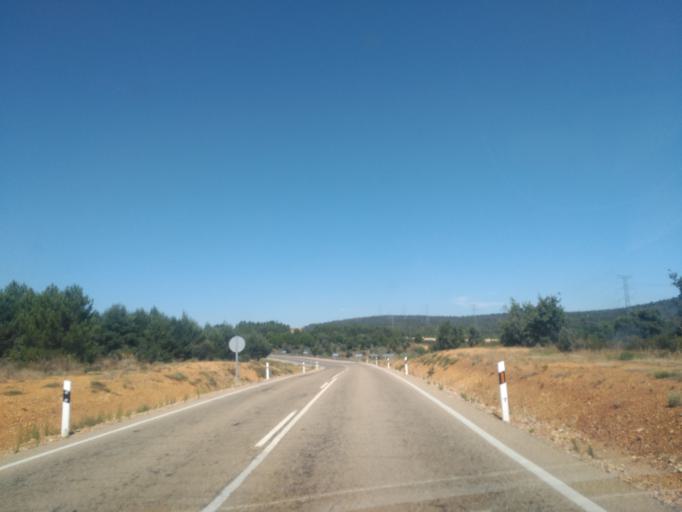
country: ES
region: Castille and Leon
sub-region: Provincia de Zamora
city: Ferreras de Abajo
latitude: 41.8978
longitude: -6.0423
